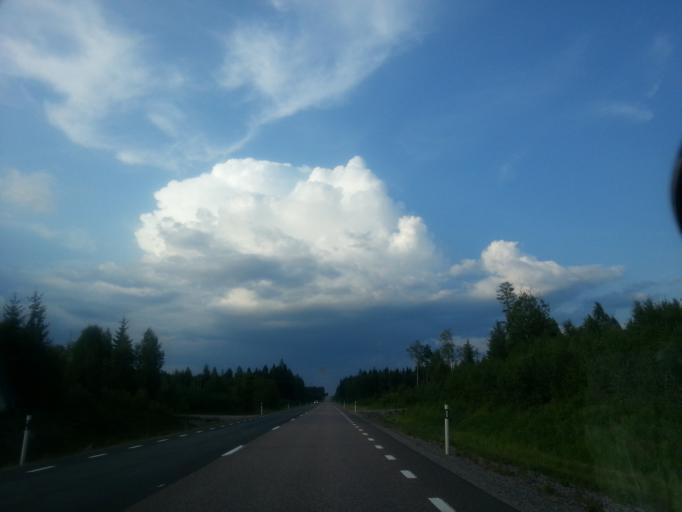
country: SE
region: Dalarna
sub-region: Avesta Kommun
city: Horndal
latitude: 60.3552
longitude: 16.4140
